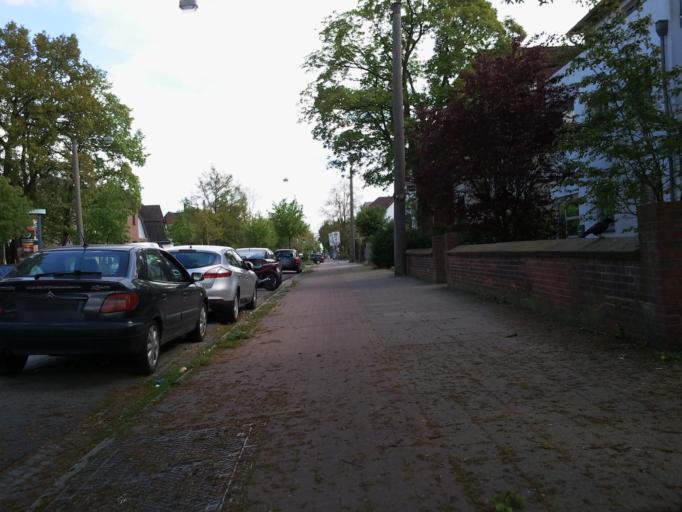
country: DE
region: Lower Saxony
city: Ritterhude
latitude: 53.1280
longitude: 8.7451
